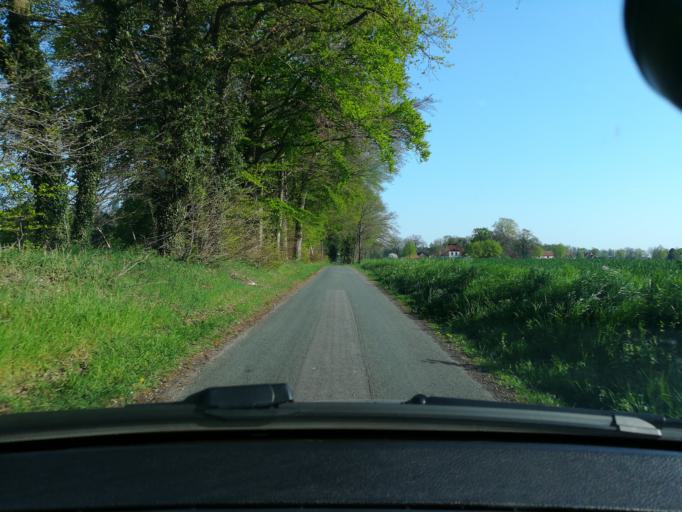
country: DE
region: North Rhine-Westphalia
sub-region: Regierungsbezirk Munster
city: Sassenberg
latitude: 52.0112
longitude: 8.0927
